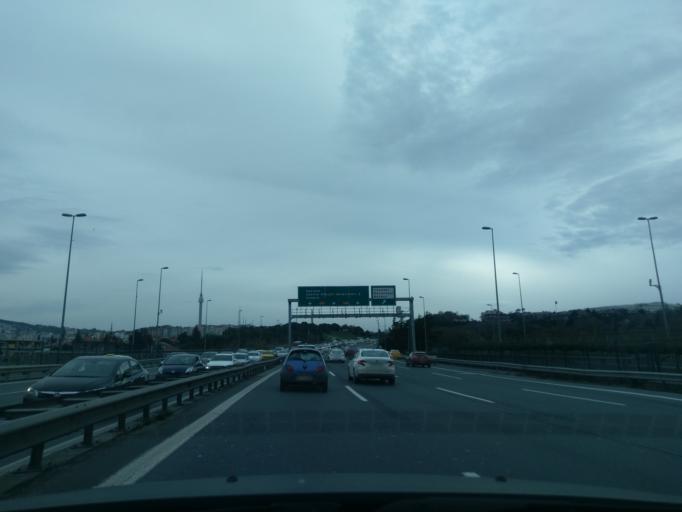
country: TR
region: Istanbul
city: UEskuedar
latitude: 41.0367
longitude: 29.0433
